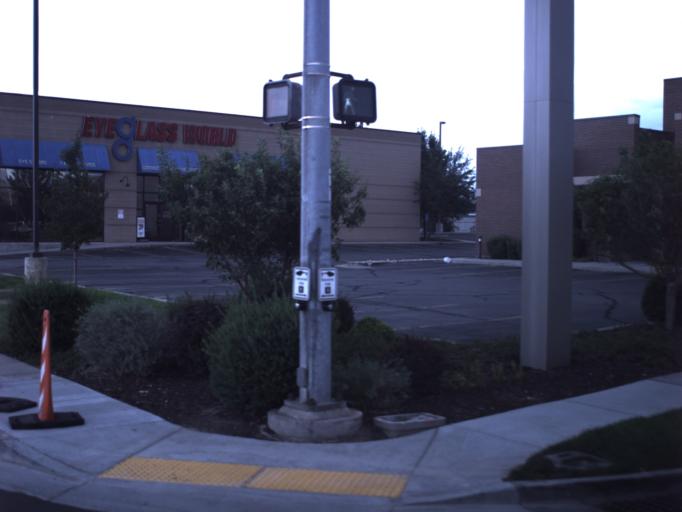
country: US
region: Utah
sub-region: Salt Lake County
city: Murray
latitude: 40.6385
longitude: -111.8890
